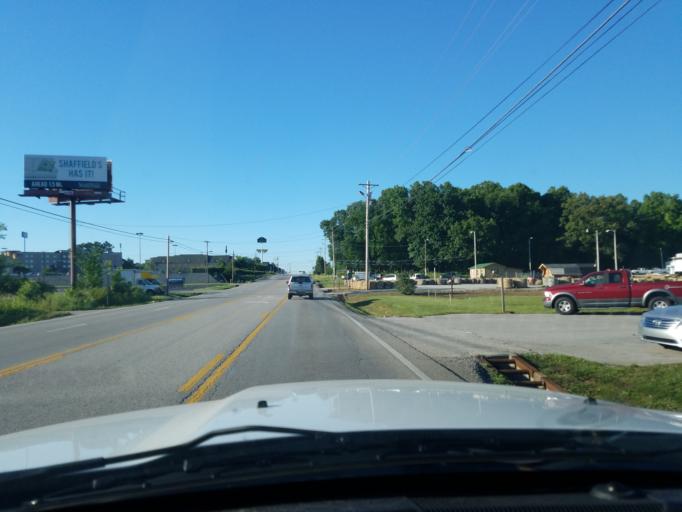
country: US
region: Tennessee
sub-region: Putnam County
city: Cookeville
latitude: 36.1294
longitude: -85.5052
